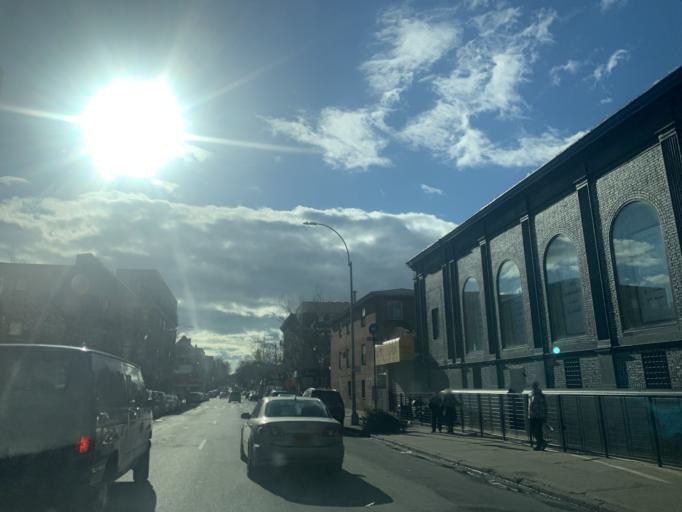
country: US
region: New York
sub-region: Kings County
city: Brooklyn
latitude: 40.6926
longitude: -73.9400
